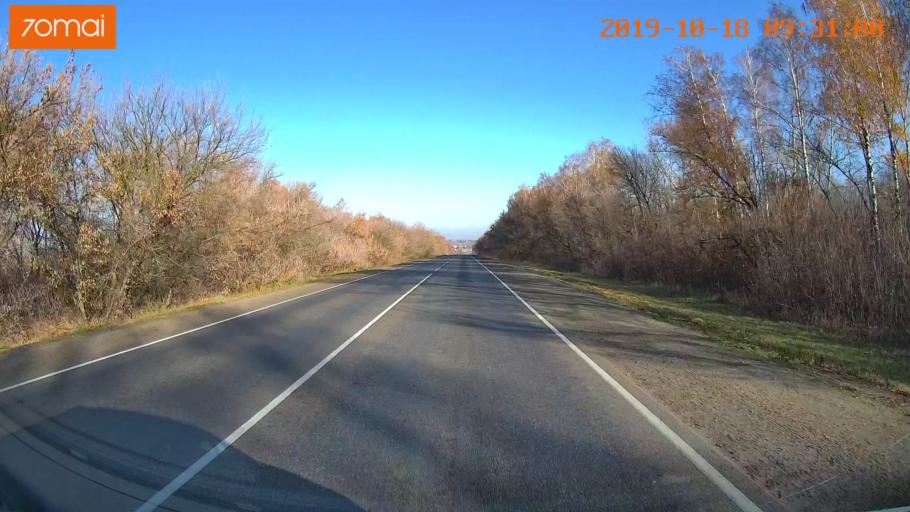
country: RU
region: Tula
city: Yefremov
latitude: 53.1453
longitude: 38.1587
